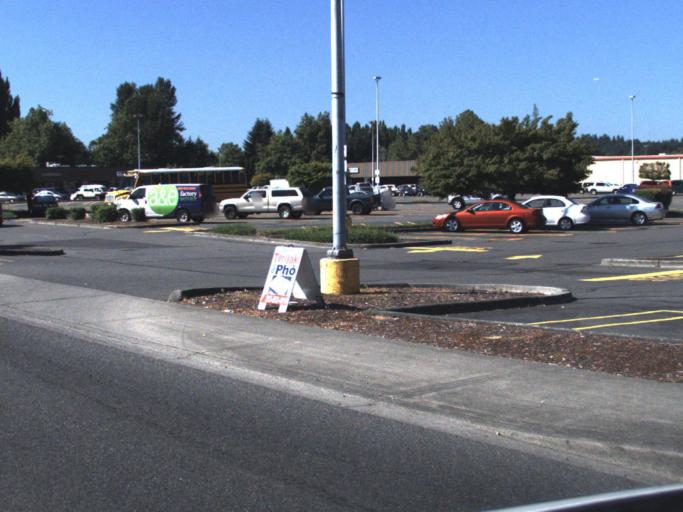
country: US
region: Washington
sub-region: King County
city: Kent
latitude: 47.3801
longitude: -122.2473
